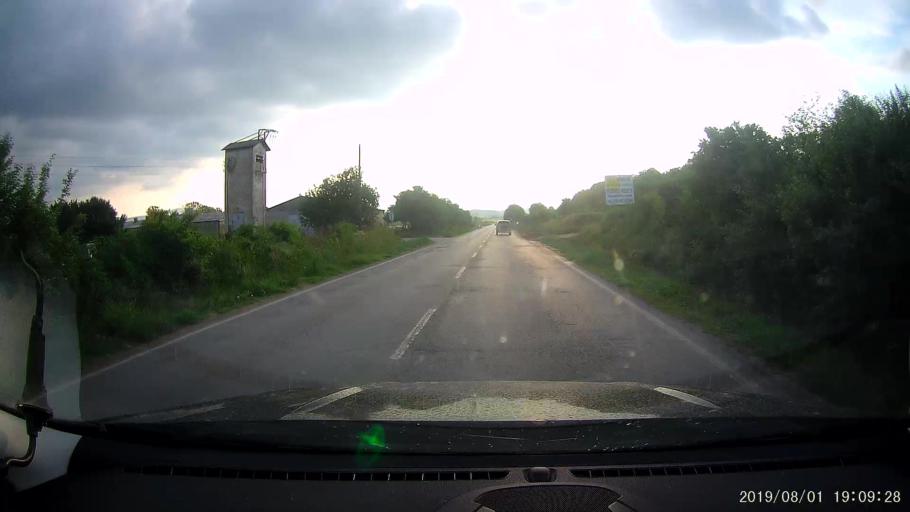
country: BG
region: Shumen
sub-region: Obshtina Smyadovo
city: Smyadovo
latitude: 42.9844
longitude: 27.0030
